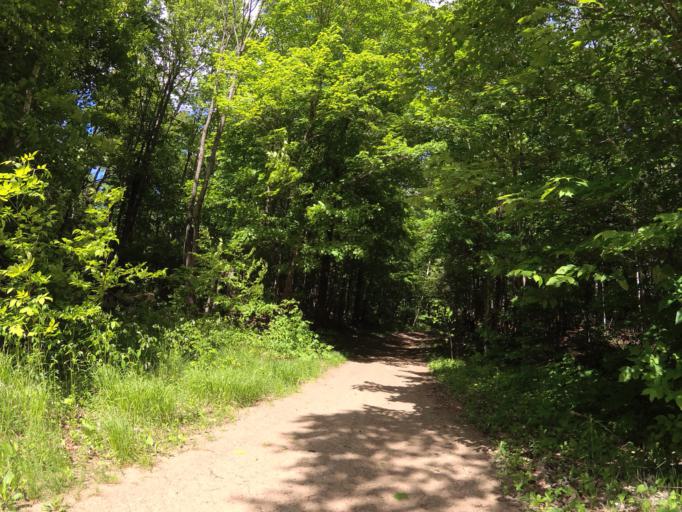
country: CA
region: Ontario
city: Renfrew
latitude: 45.0458
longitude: -76.8262
